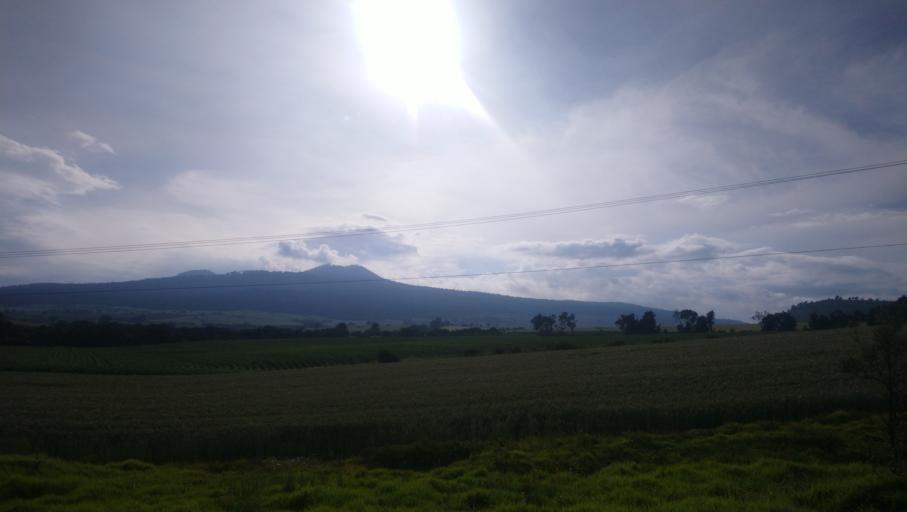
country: MX
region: Mexico
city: Juchitepec de Mariano Riva Palacio
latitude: 19.1133
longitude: -98.9364
